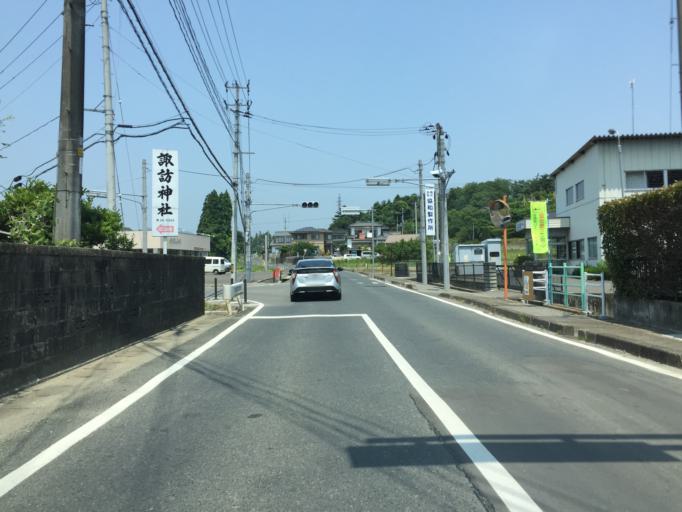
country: JP
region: Miyagi
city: Marumori
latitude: 37.8151
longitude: 140.8985
